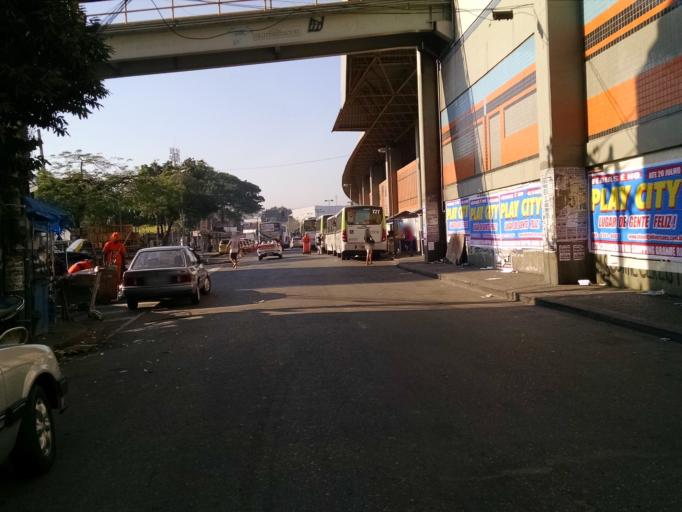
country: BR
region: Rio de Janeiro
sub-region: Sao Joao De Meriti
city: Sao Joao de Meriti
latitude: -22.8061
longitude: -43.3655
